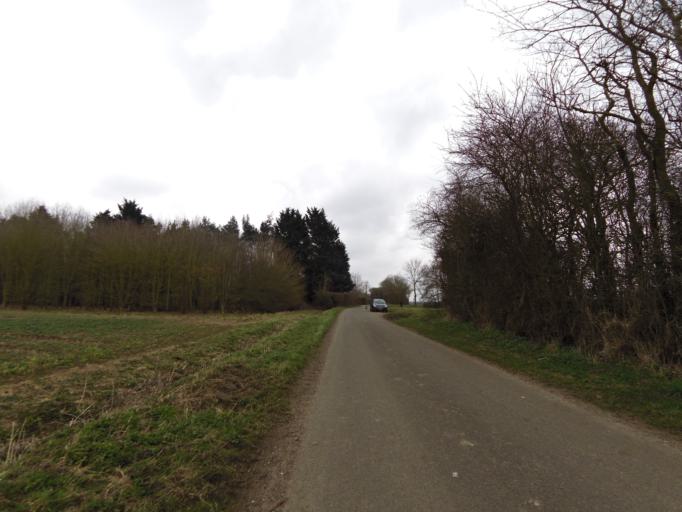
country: GB
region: England
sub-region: Suffolk
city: Halesworth
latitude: 52.3799
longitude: 1.5178
